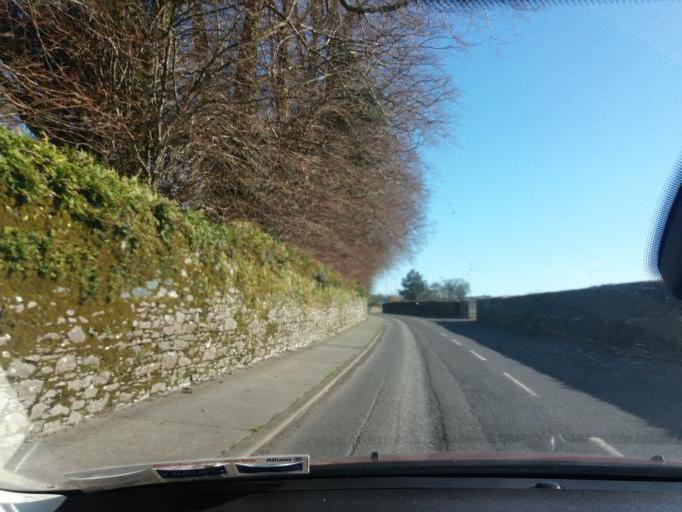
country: IE
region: Munster
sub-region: Ciarrai
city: Cill Airne
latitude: 52.0498
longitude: -9.5180
